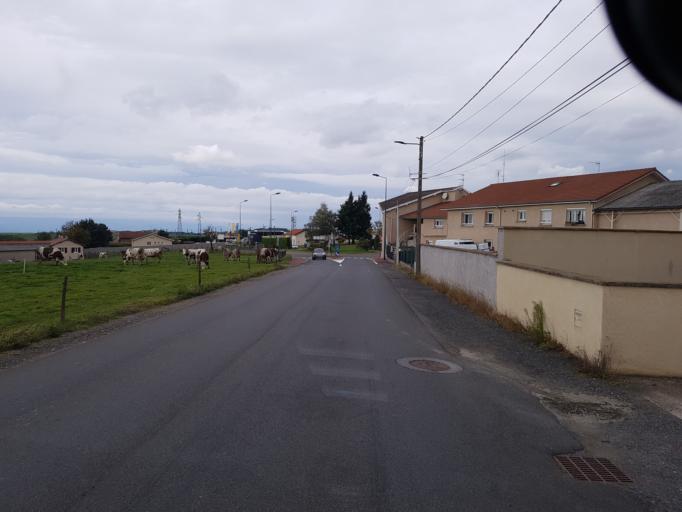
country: FR
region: Rhone-Alpes
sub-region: Departement de la Loire
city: Chazelles-sur-Lyon
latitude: 45.6349
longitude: 4.3800
